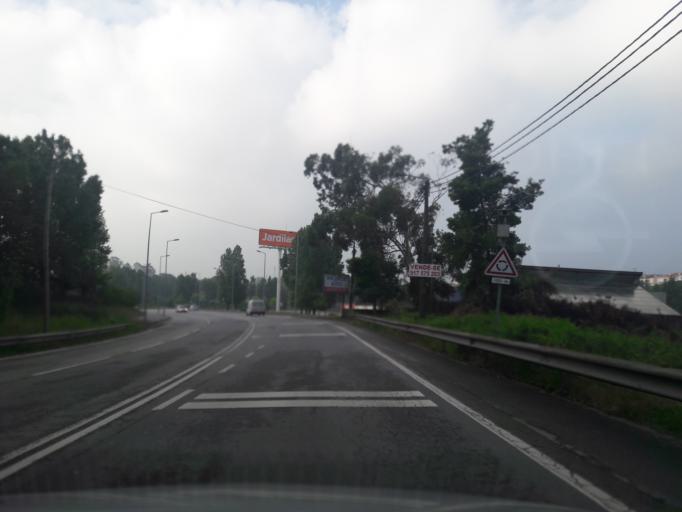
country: PT
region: Porto
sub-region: Maia
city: Maia
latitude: 41.2281
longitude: -8.6354
